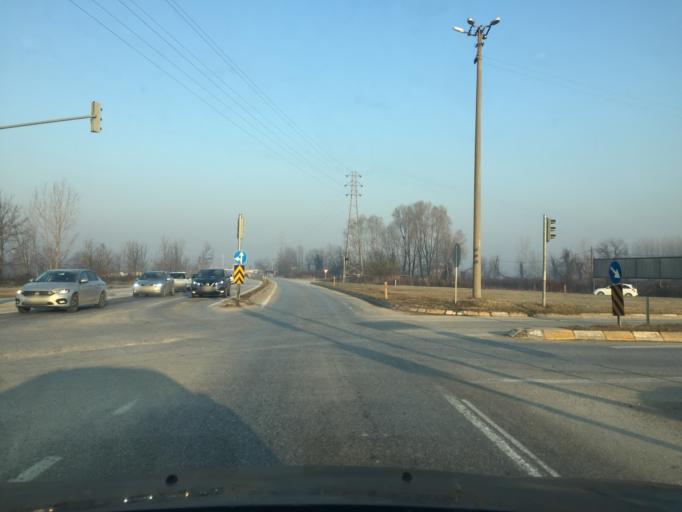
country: TR
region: Sakarya
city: Akyazi
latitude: 40.6741
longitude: 30.5860
